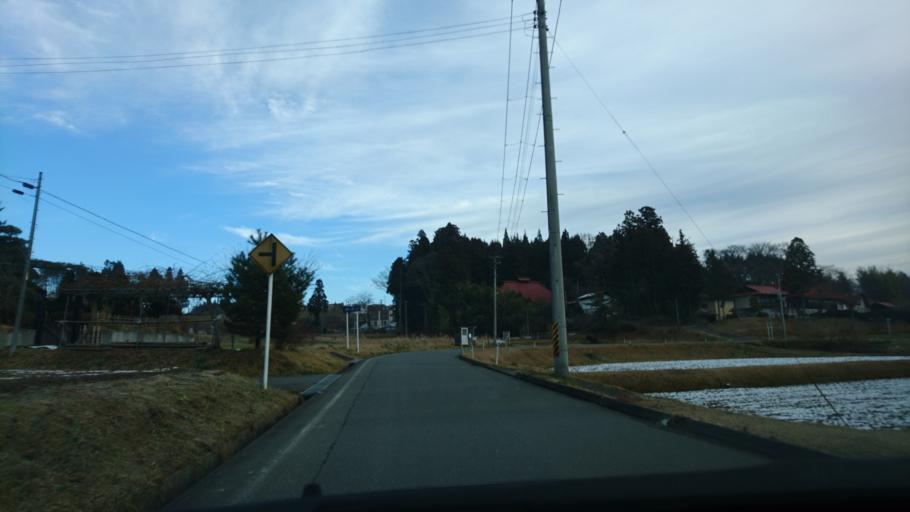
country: JP
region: Iwate
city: Ichinoseki
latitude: 38.9076
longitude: 141.3334
